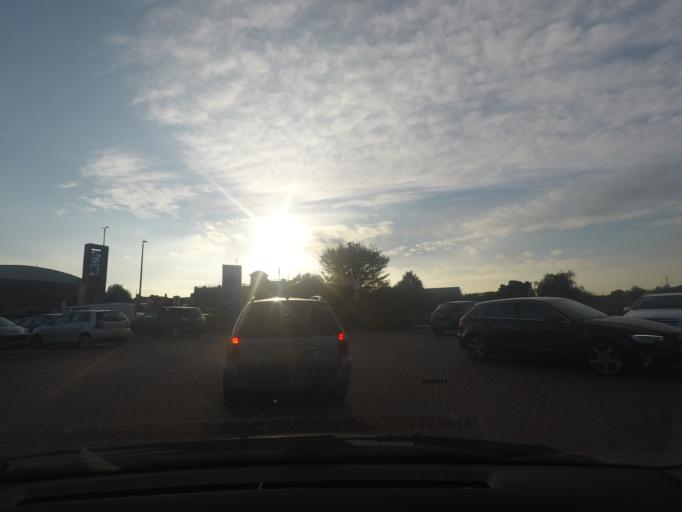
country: GB
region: England
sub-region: North East Lincolnshire
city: Grimsby
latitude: 53.5677
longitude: -0.0824
